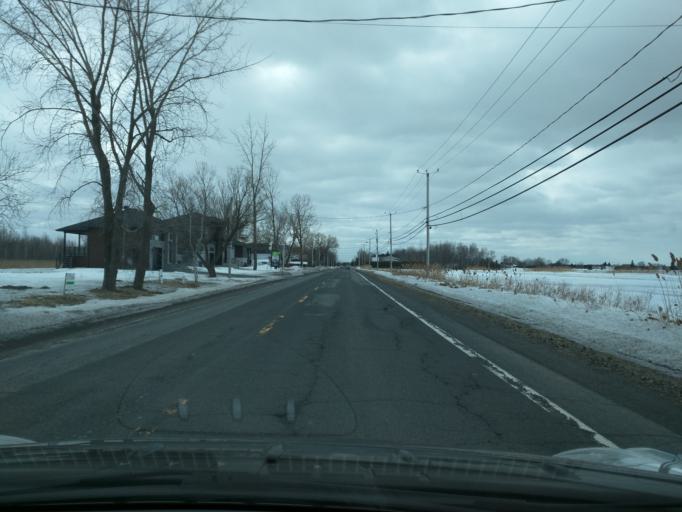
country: CA
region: Quebec
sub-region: Monteregie
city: Sainte-Julie
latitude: 45.6736
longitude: -73.2733
